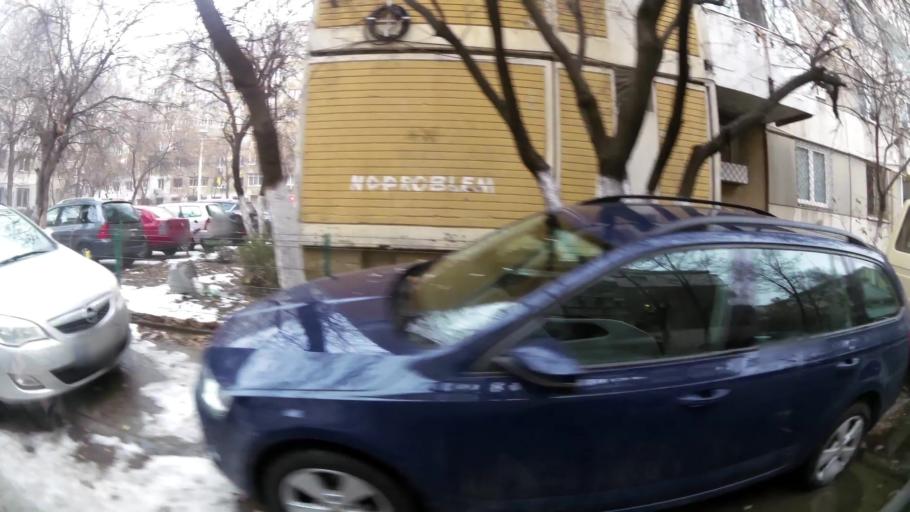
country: RO
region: Ilfov
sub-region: Comuna Chiajna
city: Rosu
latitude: 44.4555
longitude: 26.0491
